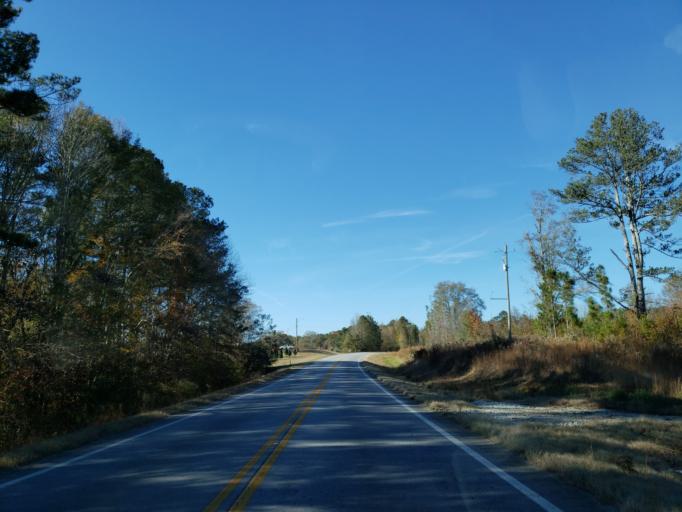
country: US
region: Alabama
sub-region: Calhoun County
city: Choccolocco
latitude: 33.5584
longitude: -85.6595
